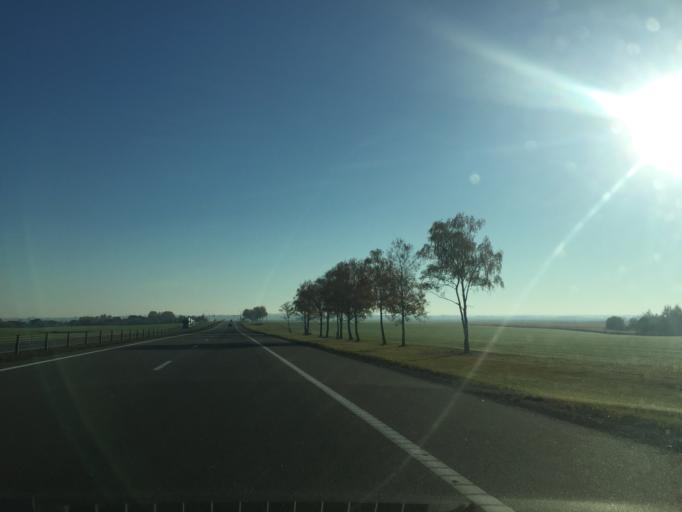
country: BY
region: Minsk
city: Zamostochcha
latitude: 53.7616
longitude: 27.9220
